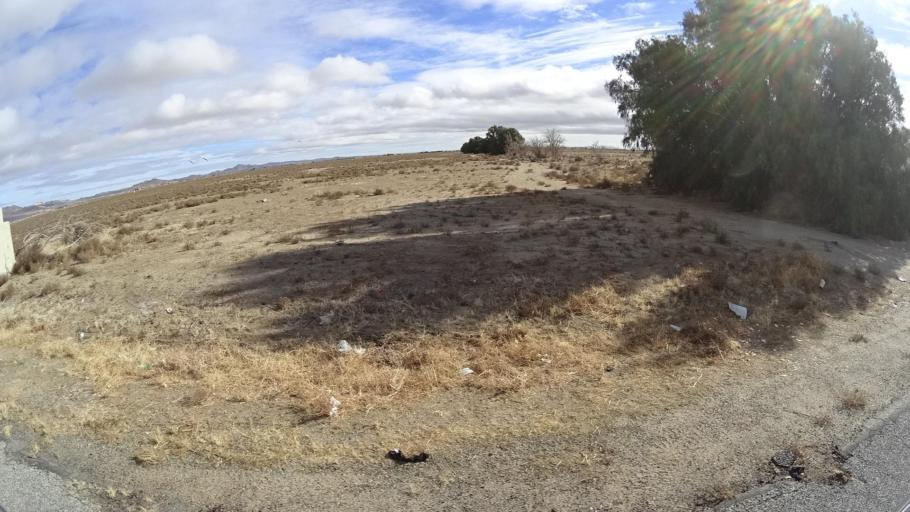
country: US
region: California
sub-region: Kern County
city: Rosamond
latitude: 34.8275
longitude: -118.3087
